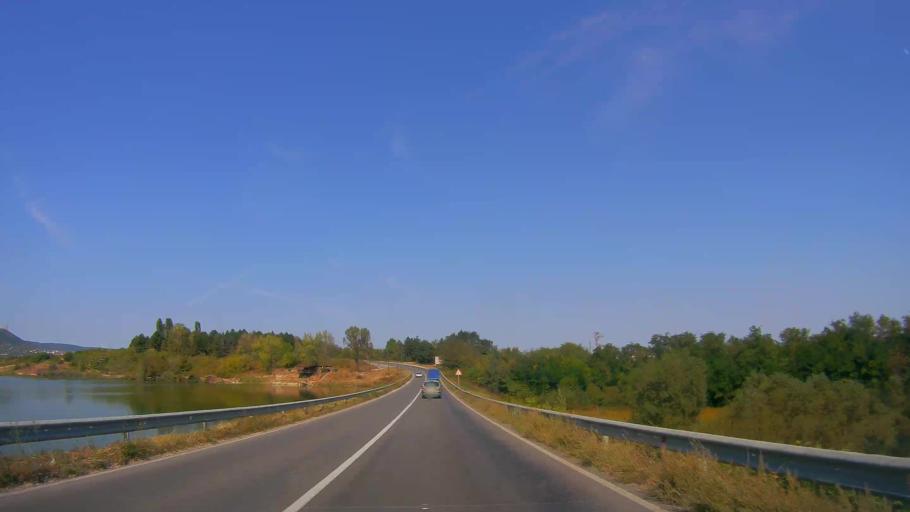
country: BG
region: Shumen
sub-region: Obshtina Shumen
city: Shumen
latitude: 43.2400
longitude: 26.9811
